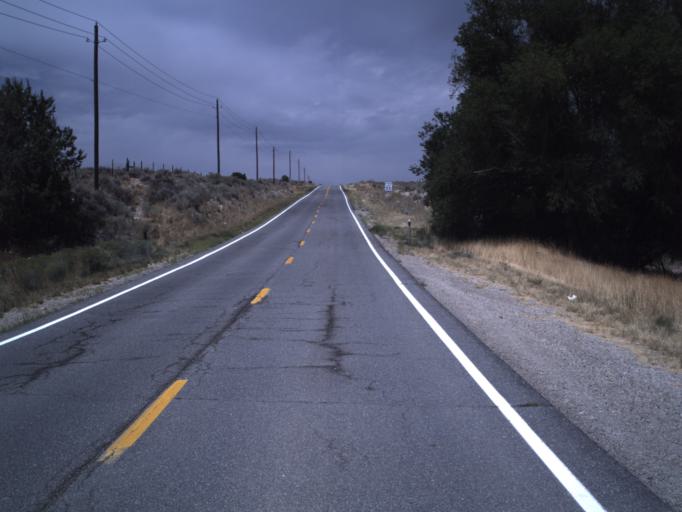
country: US
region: Utah
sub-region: Tooele County
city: Tooele
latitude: 40.3442
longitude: -112.3053
